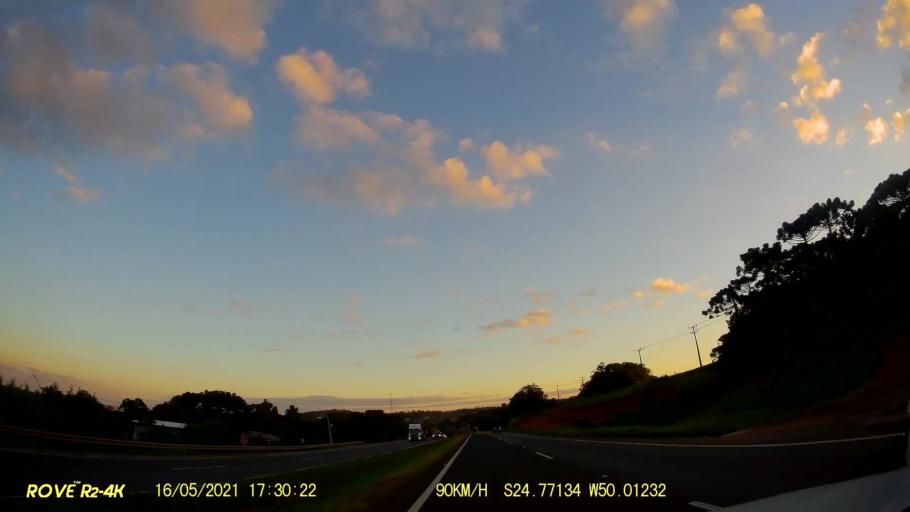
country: BR
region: Parana
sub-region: Castro
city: Castro
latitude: -24.7722
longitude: -50.0129
